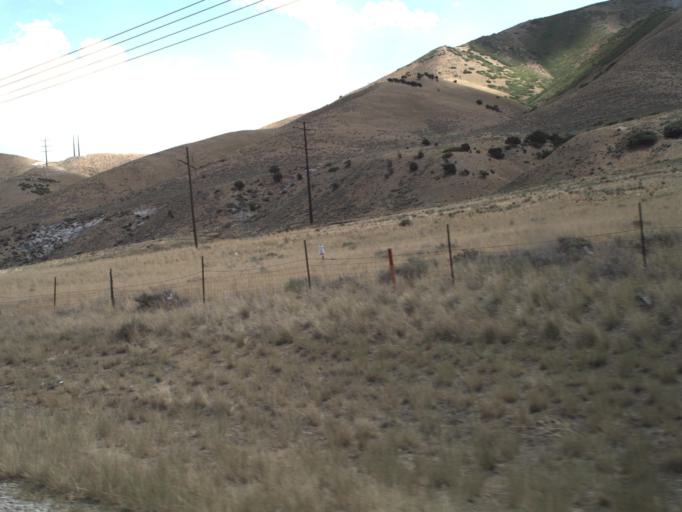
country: US
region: Utah
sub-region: Tooele County
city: Tooele
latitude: 40.4980
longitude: -112.3268
